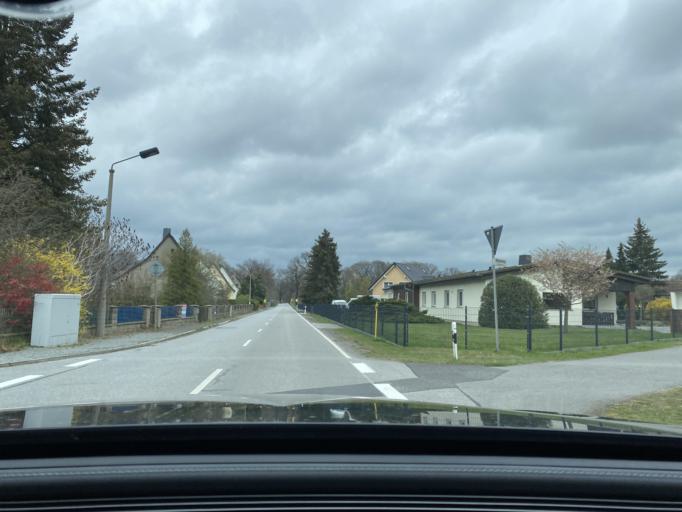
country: DE
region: Saxony
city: Neschwitz
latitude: 51.2668
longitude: 14.3354
